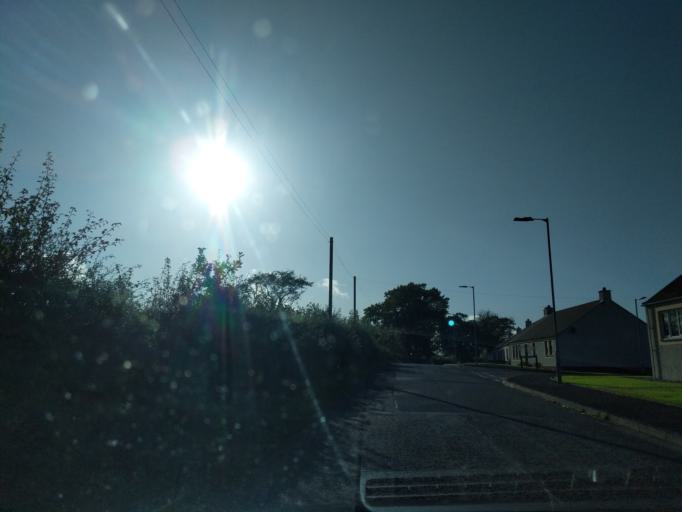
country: GB
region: Scotland
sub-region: Dumfries and Galloway
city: Dumfries
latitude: 55.0444
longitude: -3.7263
